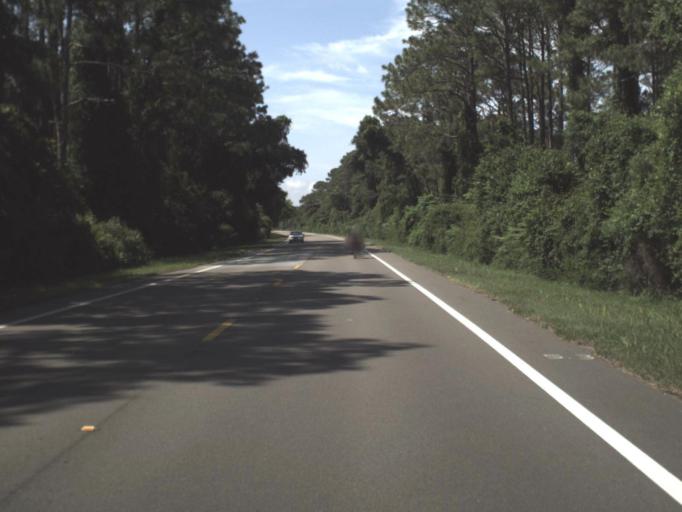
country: US
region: Florida
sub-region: Duval County
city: Atlantic Beach
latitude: 30.4861
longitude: -81.4400
